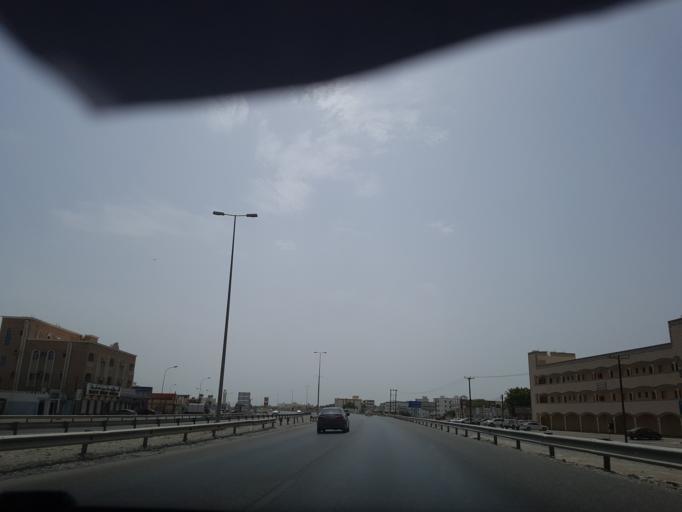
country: OM
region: Al Batinah
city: As Suwayq
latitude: 23.7454
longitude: 57.6198
